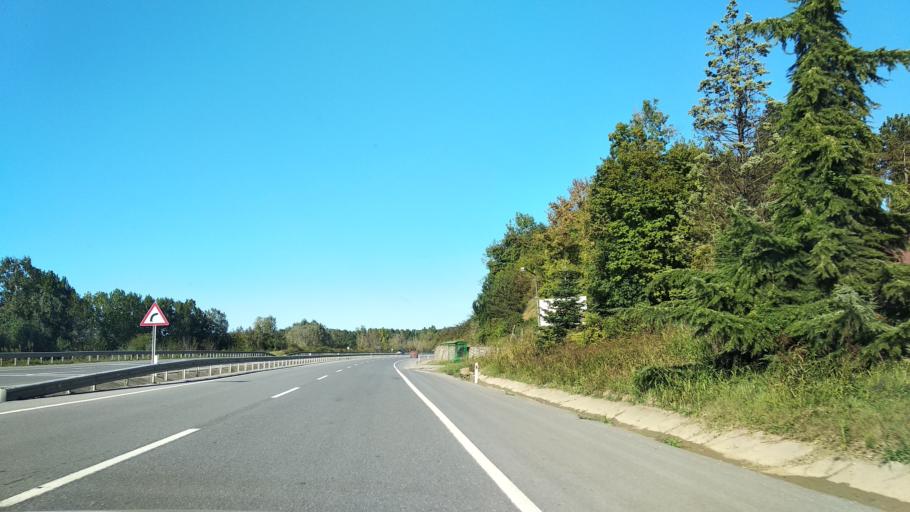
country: TR
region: Sakarya
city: Ortakoy
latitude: 41.0342
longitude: 30.6172
